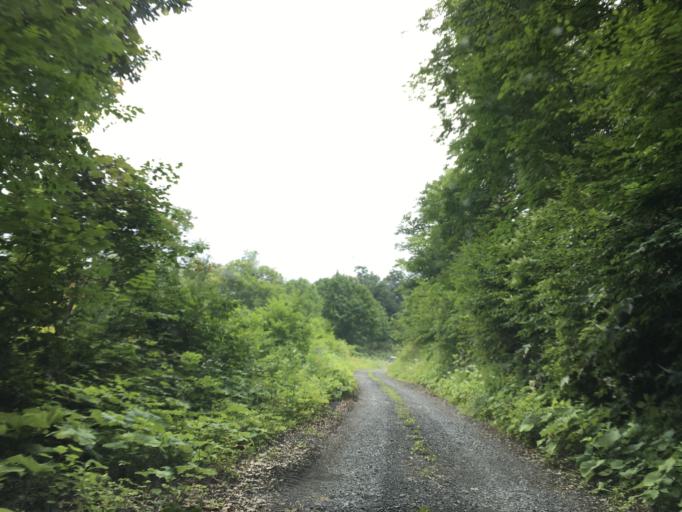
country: JP
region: Iwate
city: Ichinoseki
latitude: 38.9600
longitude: 140.8464
